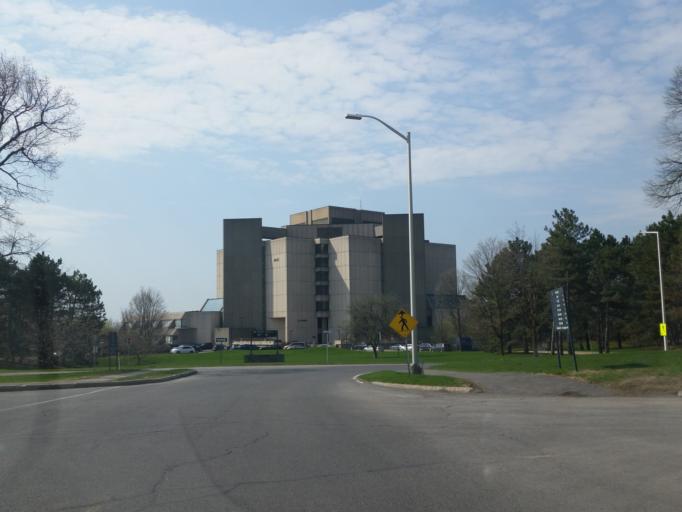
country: CA
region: Ontario
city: Ottawa
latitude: 45.4457
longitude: -75.6190
